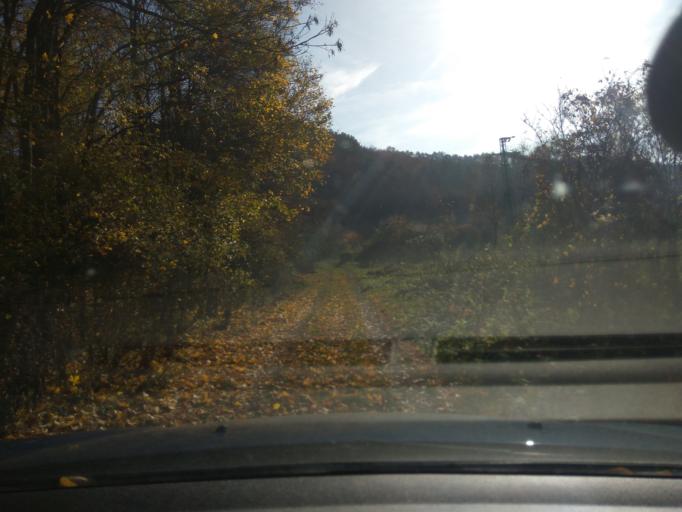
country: SK
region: Nitriansky
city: Brezova pod Bradlom
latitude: 48.6527
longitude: 17.5077
